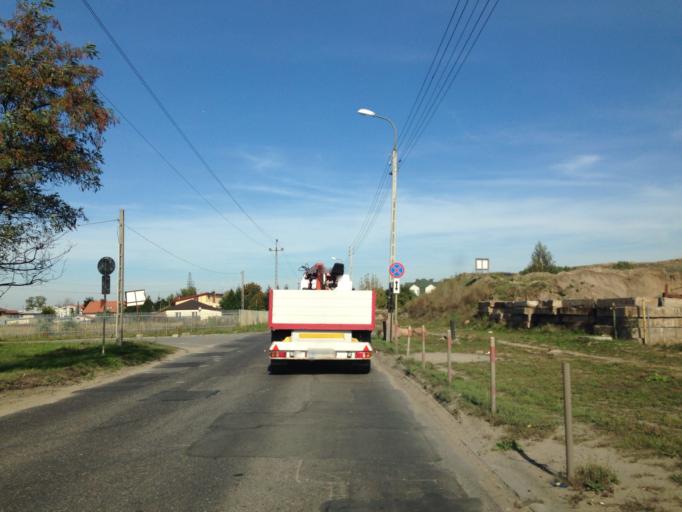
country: PL
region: Masovian Voivodeship
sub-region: Powiat pruszkowski
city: Pruszkow
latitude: 52.1731
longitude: 20.7706
